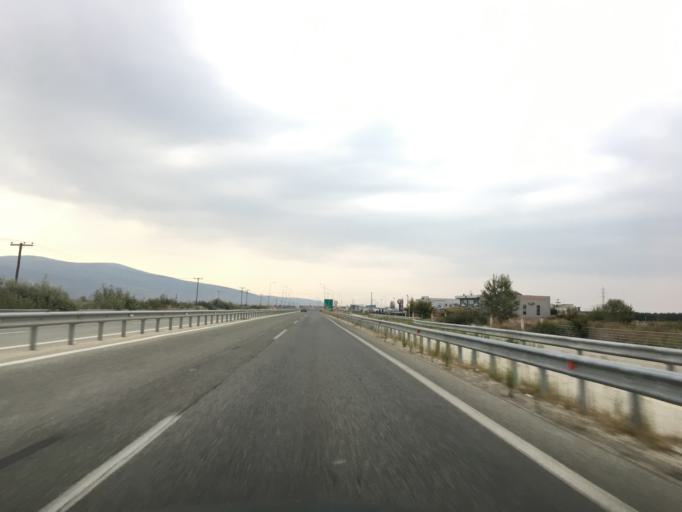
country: GR
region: Thessaly
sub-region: Trikala
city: Megalochori
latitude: 39.5664
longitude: 21.8158
